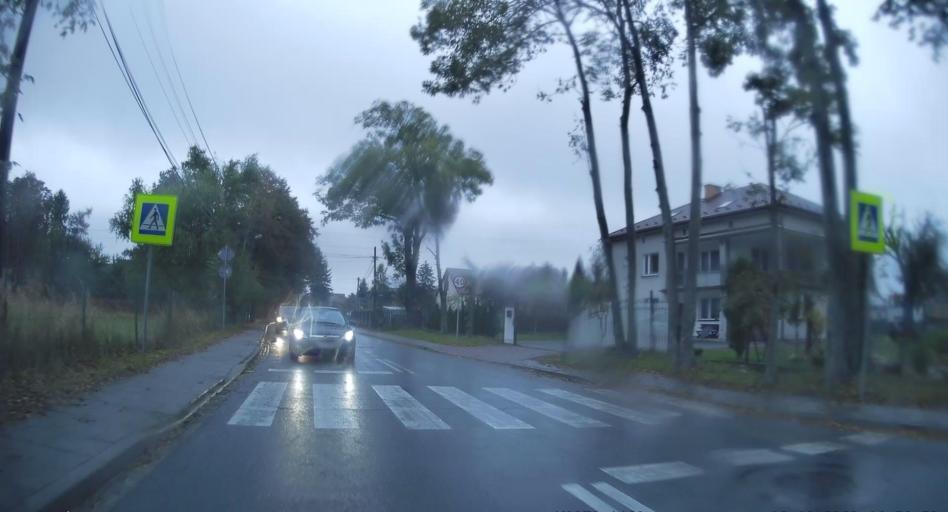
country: PL
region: Lesser Poland Voivodeship
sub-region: Powiat krakowski
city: Ochojno
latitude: 49.9802
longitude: 19.9898
